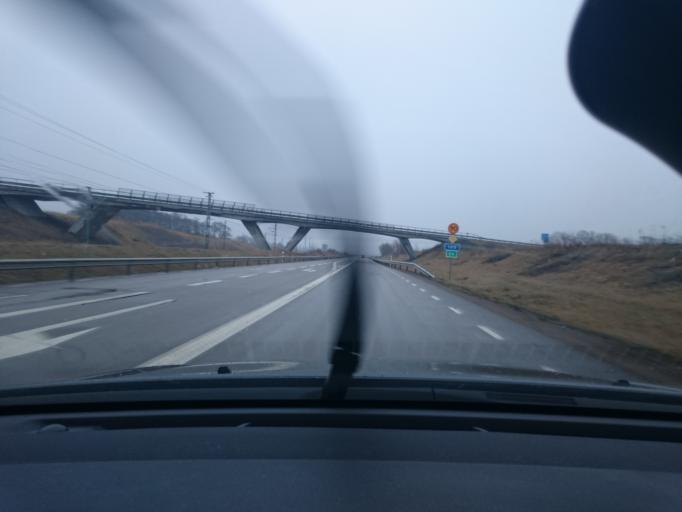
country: SE
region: Skane
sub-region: Bastads Kommun
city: Forslov
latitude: 56.3448
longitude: 12.8008
